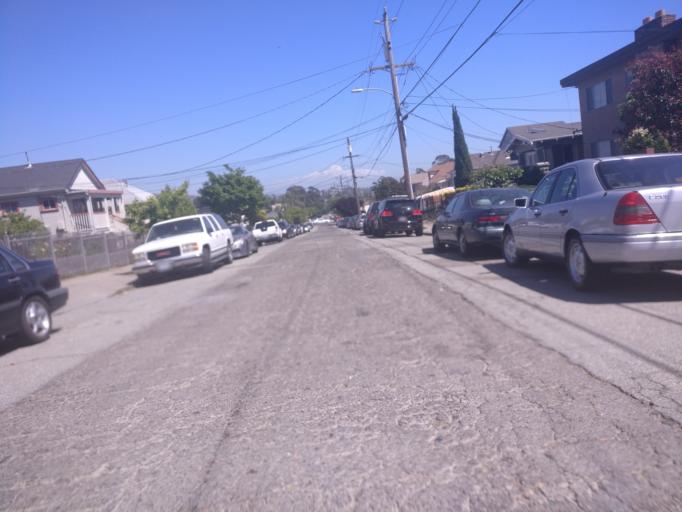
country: US
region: California
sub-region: Alameda County
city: Piedmont
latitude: 37.7925
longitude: -122.2164
